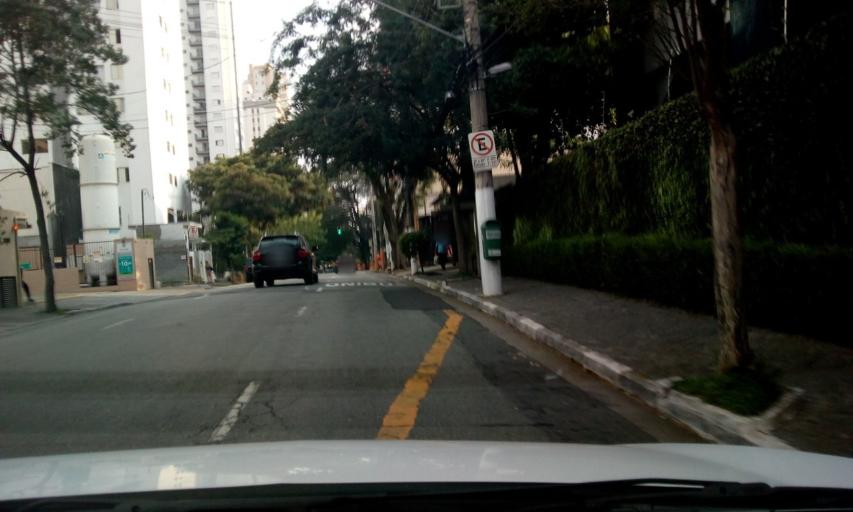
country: BR
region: Sao Paulo
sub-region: Sao Paulo
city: Sao Paulo
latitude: -23.6009
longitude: -46.6614
